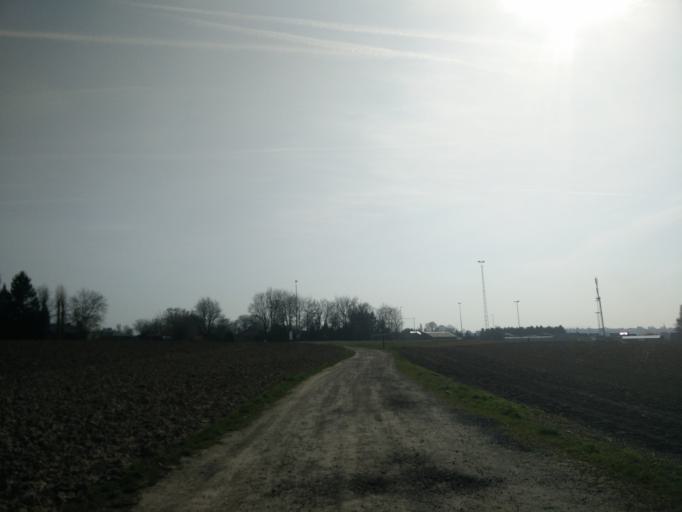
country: BE
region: Flanders
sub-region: Provincie Limburg
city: Sint-Pieters-Voeren
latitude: 50.7405
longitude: 5.7717
